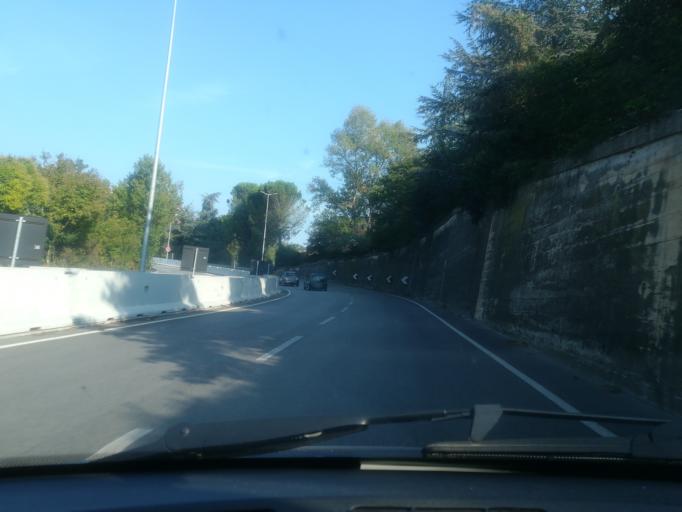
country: IT
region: The Marches
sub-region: Provincia di Macerata
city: Macerata
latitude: 43.2909
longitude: 13.4478
